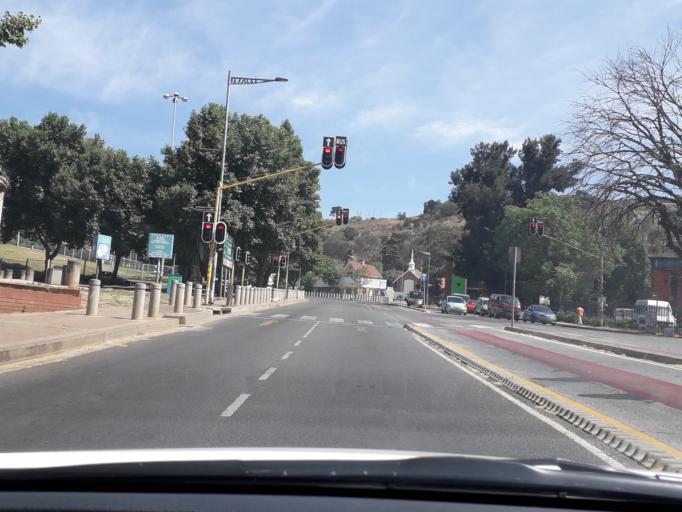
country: ZA
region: Gauteng
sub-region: City of Johannesburg Metropolitan Municipality
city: Johannesburg
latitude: -26.1926
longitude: 28.0635
